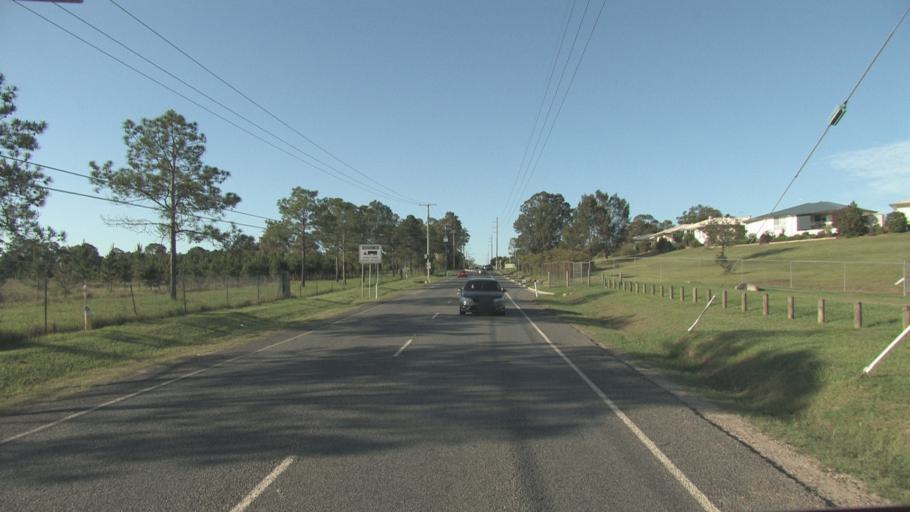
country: AU
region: Queensland
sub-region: Logan
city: Waterford West
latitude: -27.6934
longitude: 153.1193
